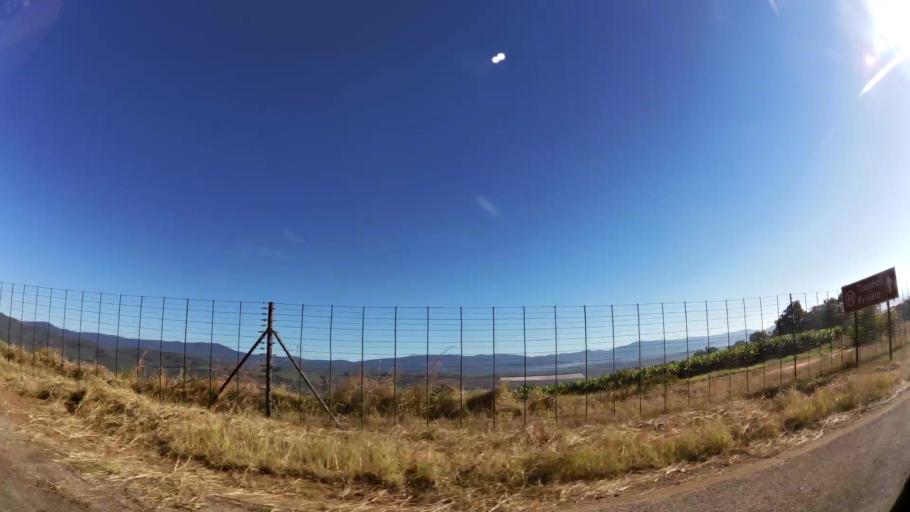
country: ZA
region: Limpopo
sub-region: Mopani District Municipality
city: Tzaneen
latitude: -23.8391
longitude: 30.1313
